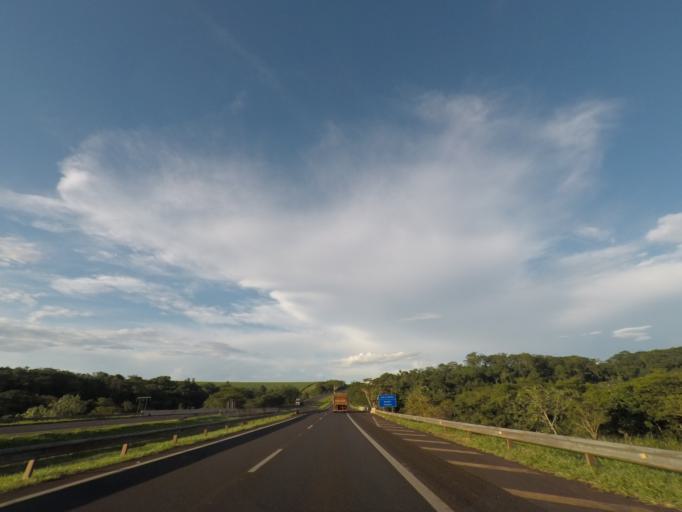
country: BR
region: Sao Paulo
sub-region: Ituverava
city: Ituverava
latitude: -20.2571
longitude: -47.7998
